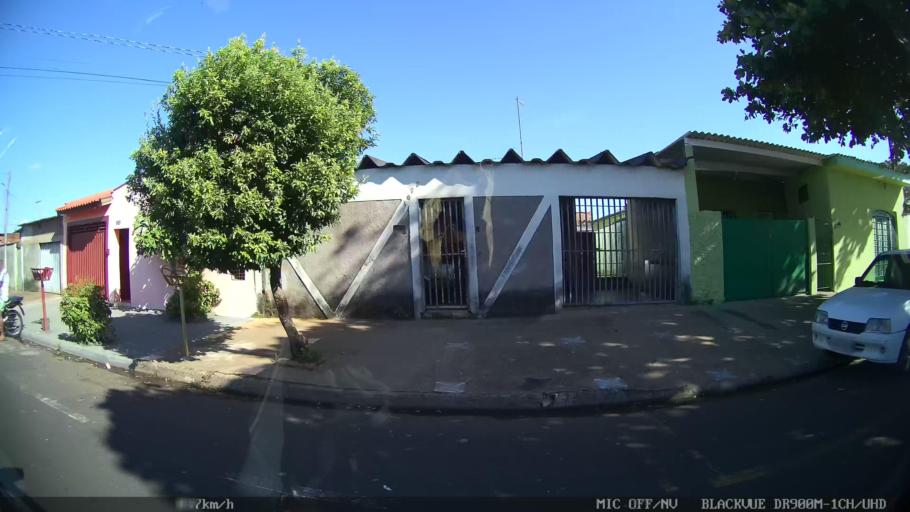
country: BR
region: Sao Paulo
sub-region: Franca
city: Franca
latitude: -20.4956
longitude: -47.4153
